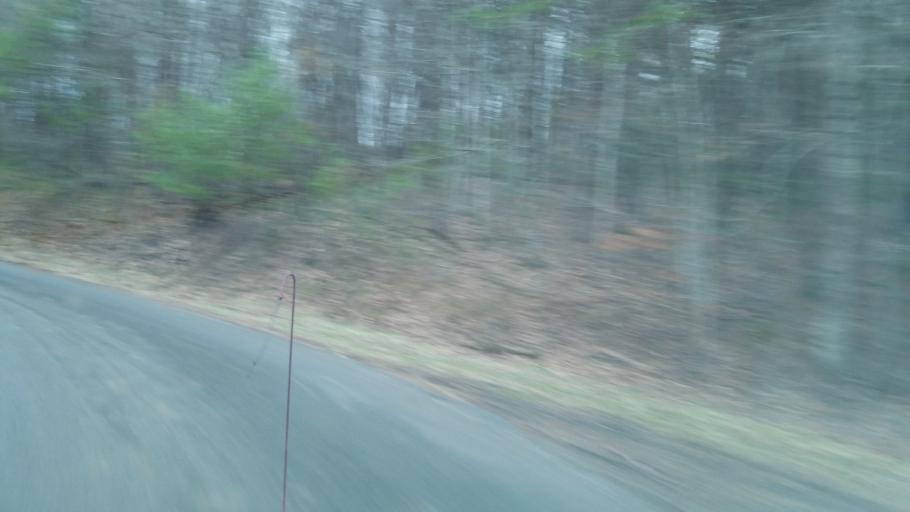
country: US
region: Virginia
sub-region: Pulaski County
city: Pulaski
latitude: 37.1703
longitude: -80.8598
